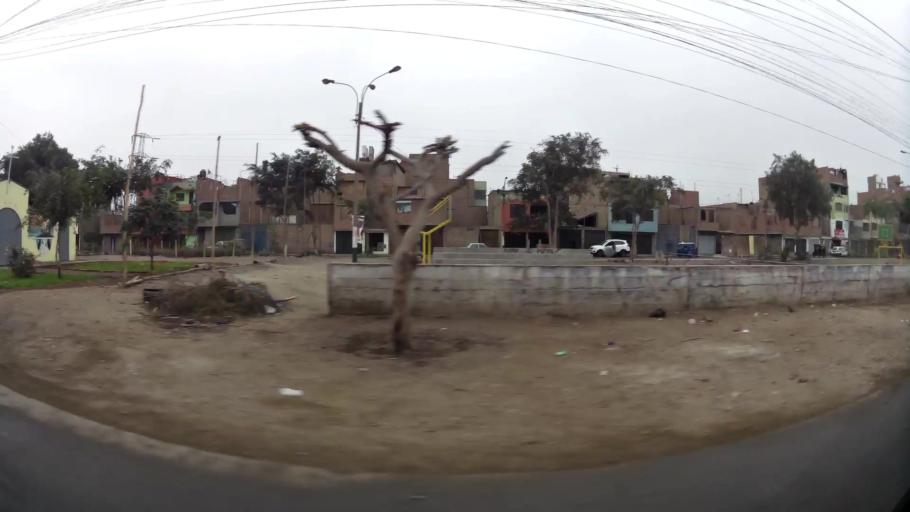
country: PE
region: Lima
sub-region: Lima
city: Independencia
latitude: -11.9699
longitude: -77.0826
